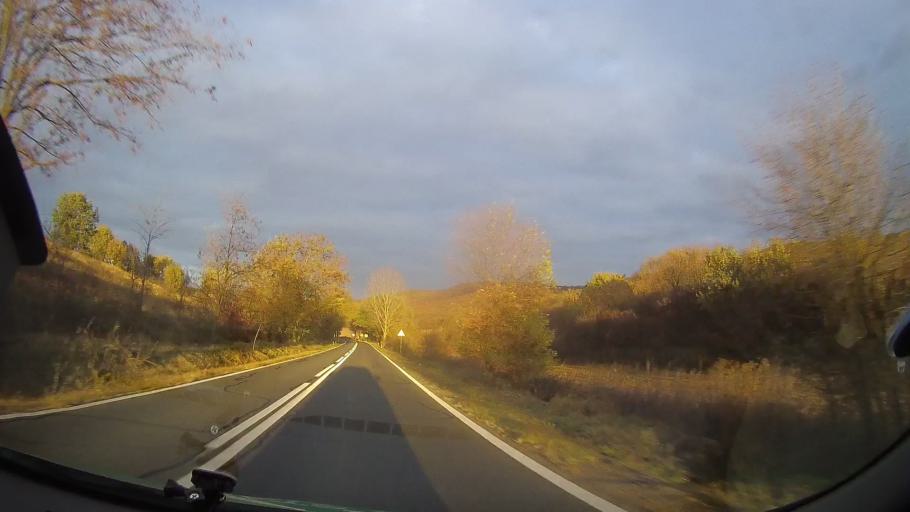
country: RO
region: Tulcea
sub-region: Comuna Ciucurova
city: Ciucurova
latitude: 44.9475
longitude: 28.5037
